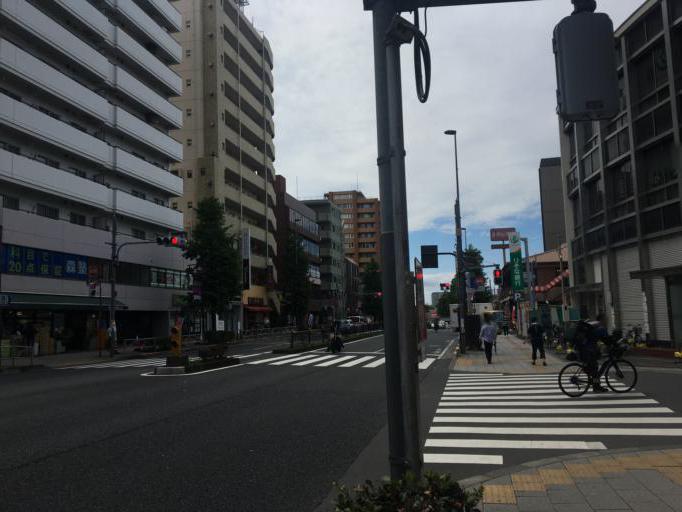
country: JP
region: Saitama
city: Wako
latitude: 35.7775
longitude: 139.6299
